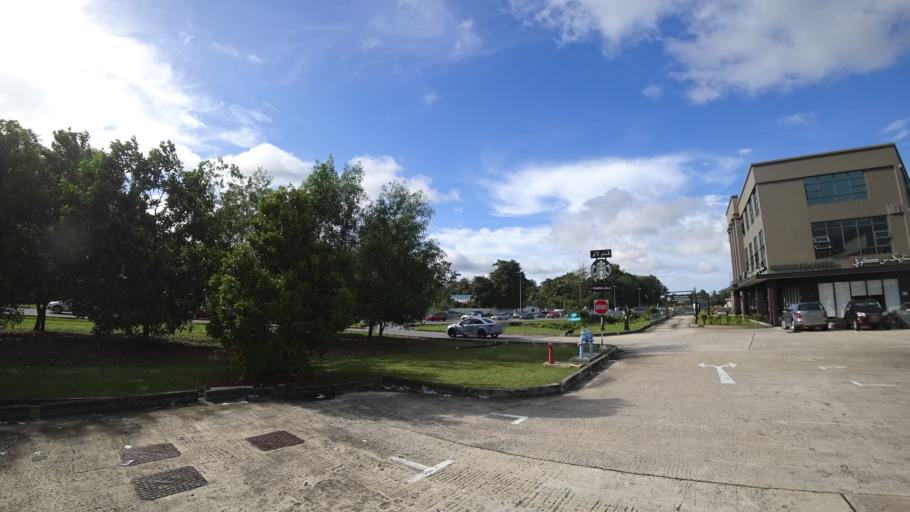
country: BN
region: Brunei and Muara
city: Bandar Seri Begawan
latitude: 4.8870
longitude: 114.8978
